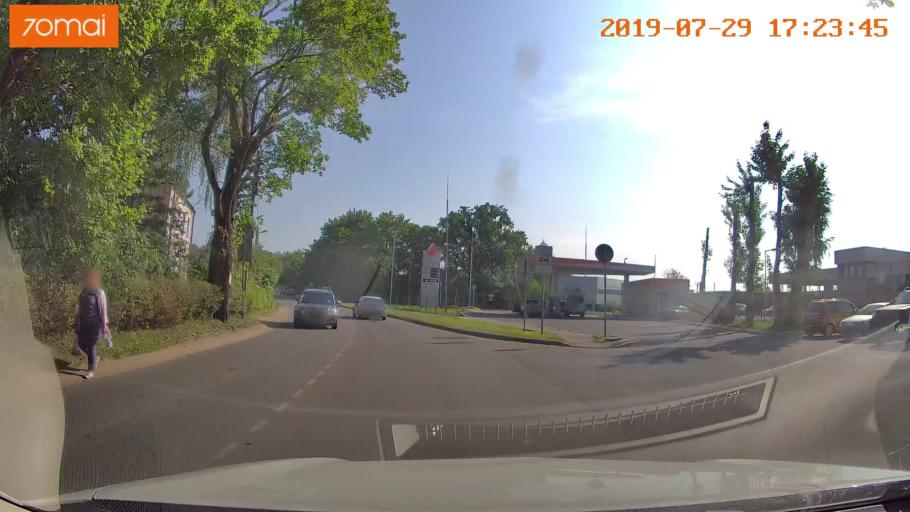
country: RU
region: Kaliningrad
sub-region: Gorod Kaliningrad
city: Kaliningrad
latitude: 54.7645
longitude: 20.4440
